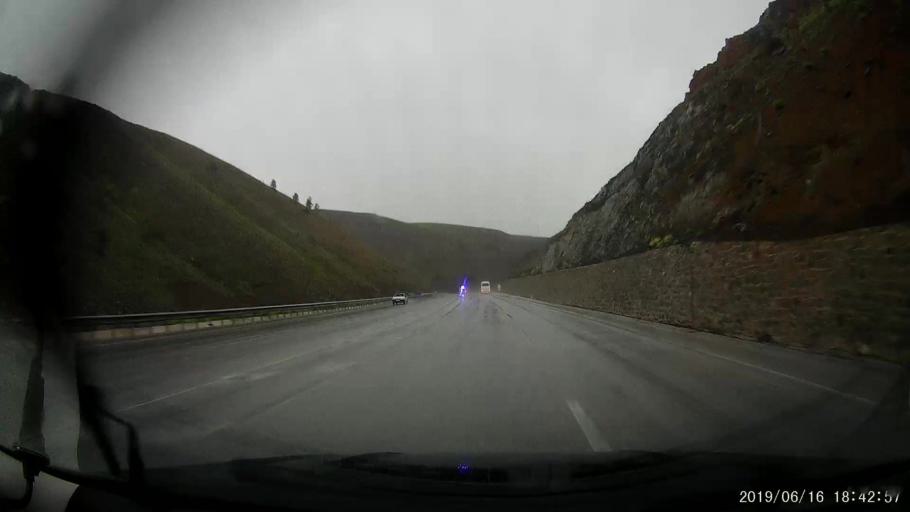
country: TR
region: Erzincan
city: Doganbeyli
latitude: 39.8680
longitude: 39.0986
